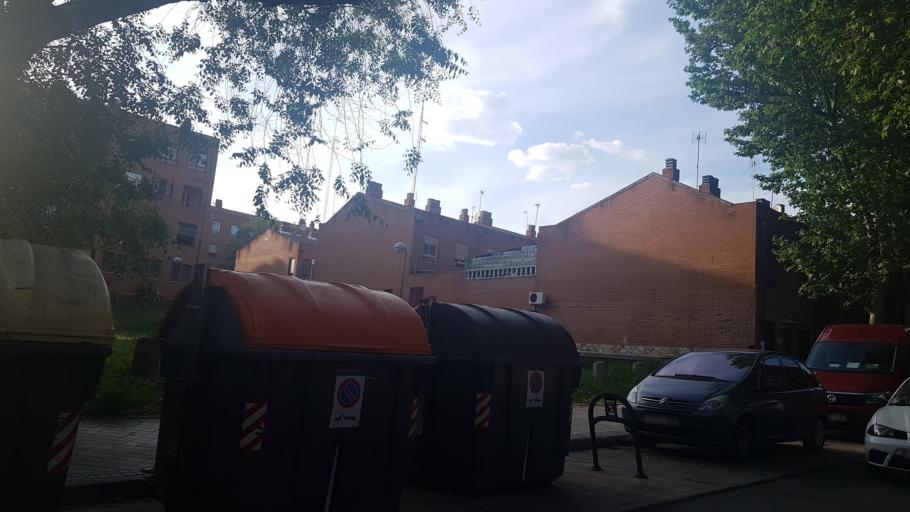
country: ES
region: Madrid
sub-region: Provincia de Madrid
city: Puente de Vallecas
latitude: 40.3698
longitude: -3.6597
